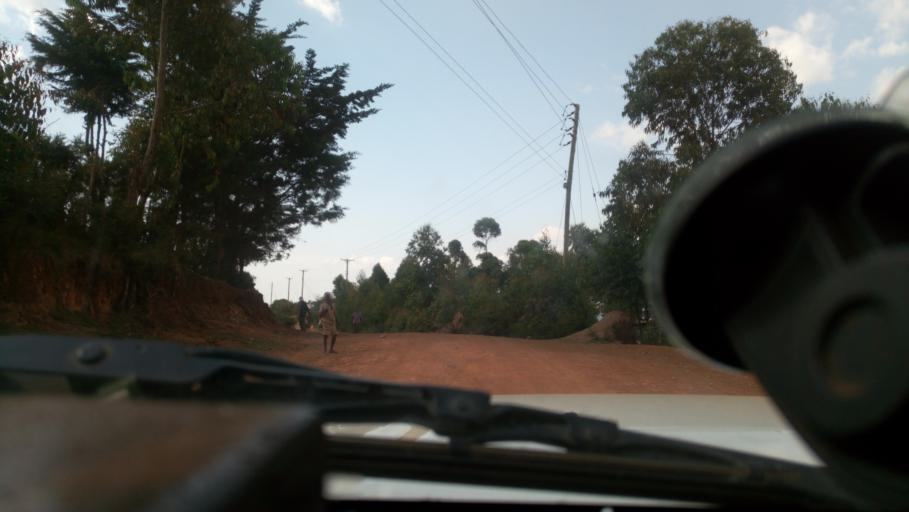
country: KE
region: Nyamira District
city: Nyamira
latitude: -0.6132
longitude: 35.0039
